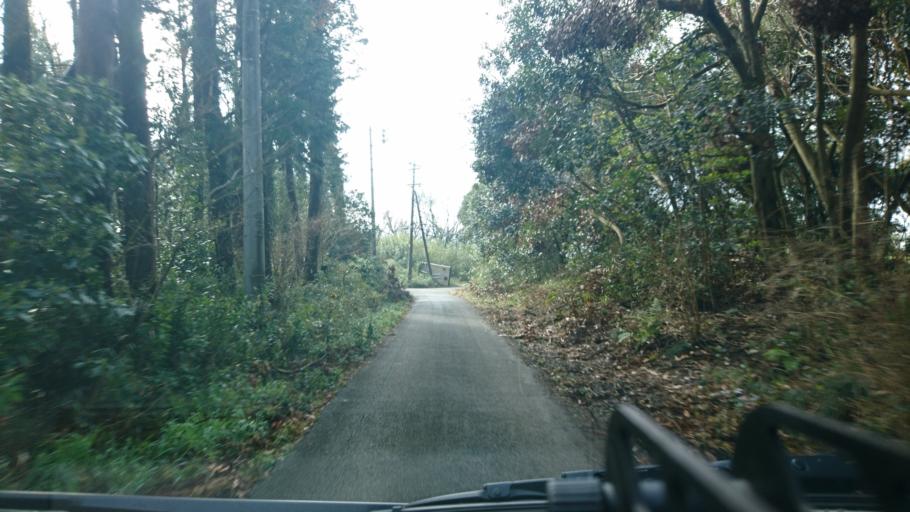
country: JP
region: Chiba
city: Kisarazu
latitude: 35.3272
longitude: 139.9659
